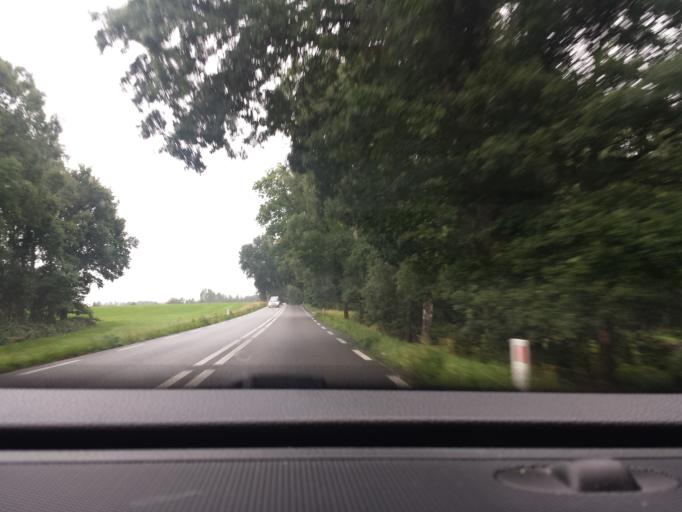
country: NL
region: Gelderland
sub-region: Gemeente Montferland
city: s-Heerenberg
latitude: 51.8895
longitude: 6.2541
